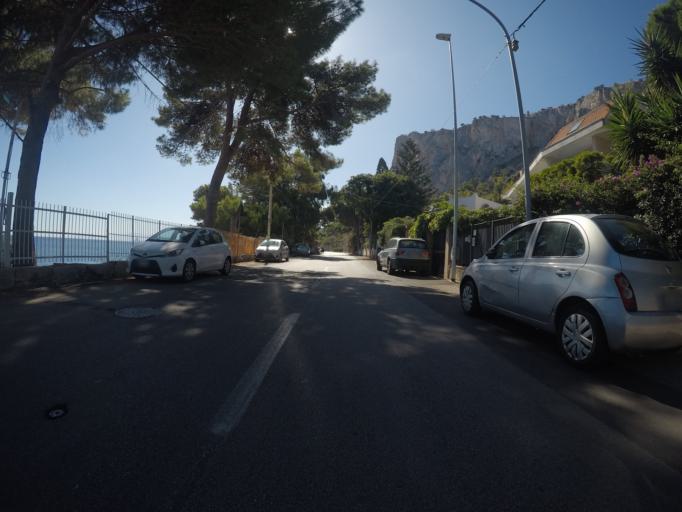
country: IT
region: Sicily
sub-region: Palermo
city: Palermo
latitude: 38.1881
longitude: 13.3598
